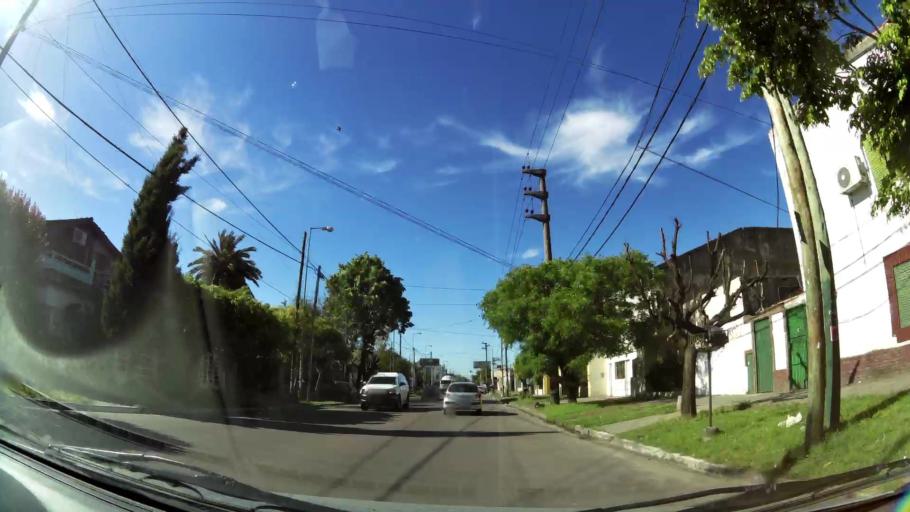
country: AR
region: Buenos Aires
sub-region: Partido de Lomas de Zamora
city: Lomas de Zamora
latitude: -34.7623
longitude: -58.4226
